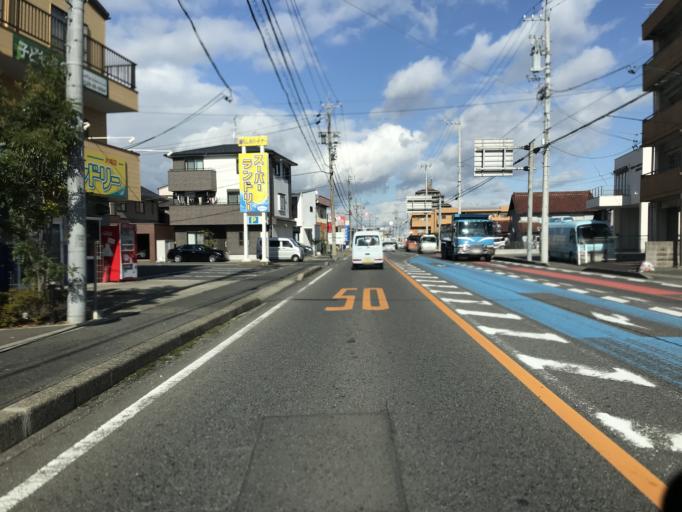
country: JP
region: Aichi
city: Komaki
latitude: 35.2437
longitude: 136.8955
